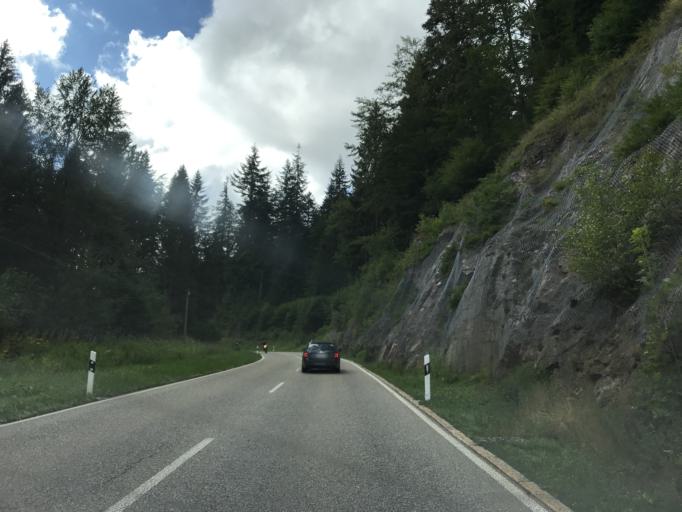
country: DE
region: Baden-Wuerttemberg
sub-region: Freiburg Region
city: Oberried
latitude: 47.8961
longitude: 7.9217
